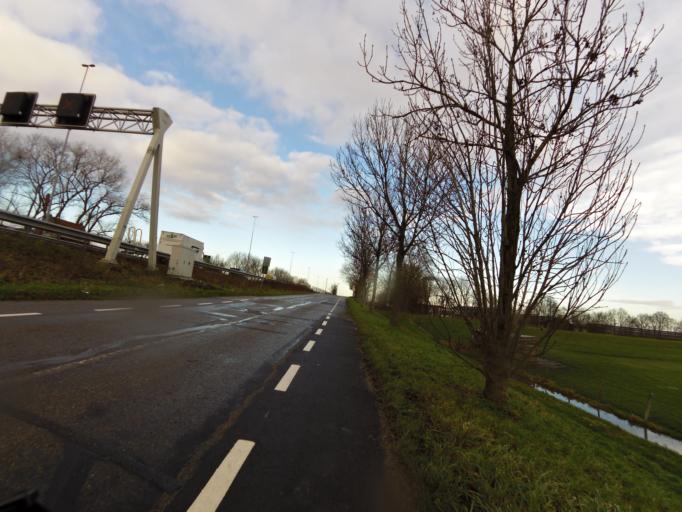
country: NL
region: South Holland
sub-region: Gemeente Schiedam
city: Schiedam
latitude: 51.9660
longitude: 4.4043
